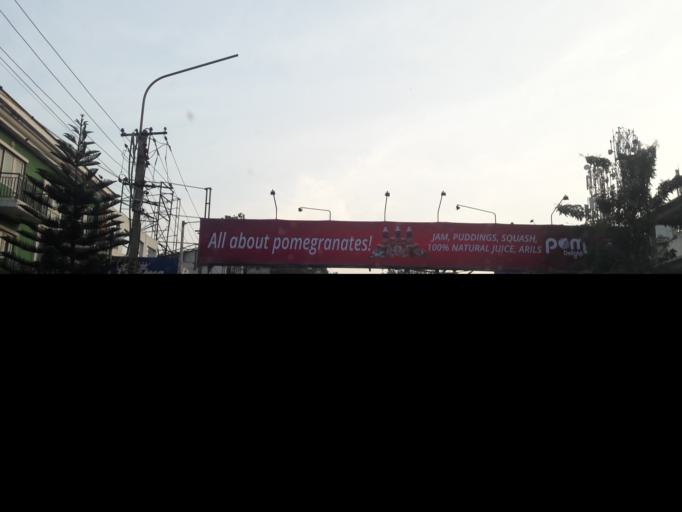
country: IN
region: Karnataka
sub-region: Bangalore Urban
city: Bangalore
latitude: 12.9652
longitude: 77.6069
